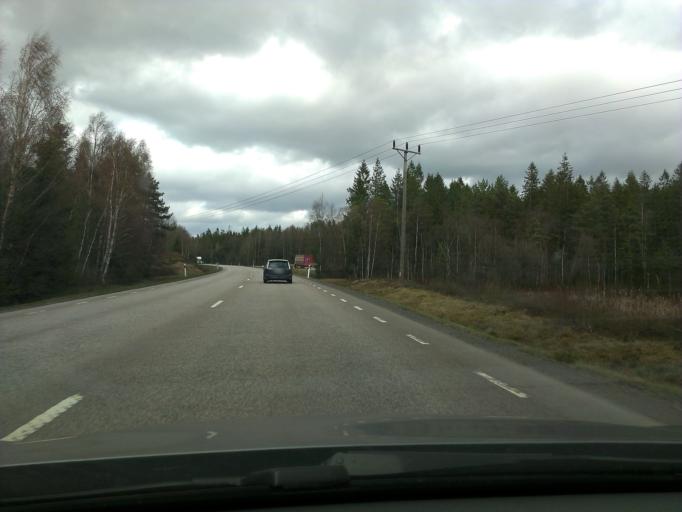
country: SE
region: Kronoberg
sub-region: Almhults Kommun
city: AElmhult
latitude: 56.5948
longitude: 14.2091
